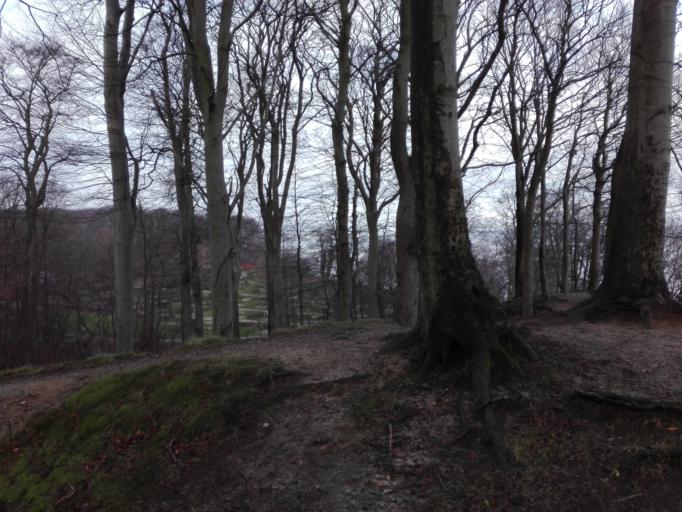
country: DK
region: Central Jutland
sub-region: Arhus Kommune
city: Beder
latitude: 56.1079
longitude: 10.2355
